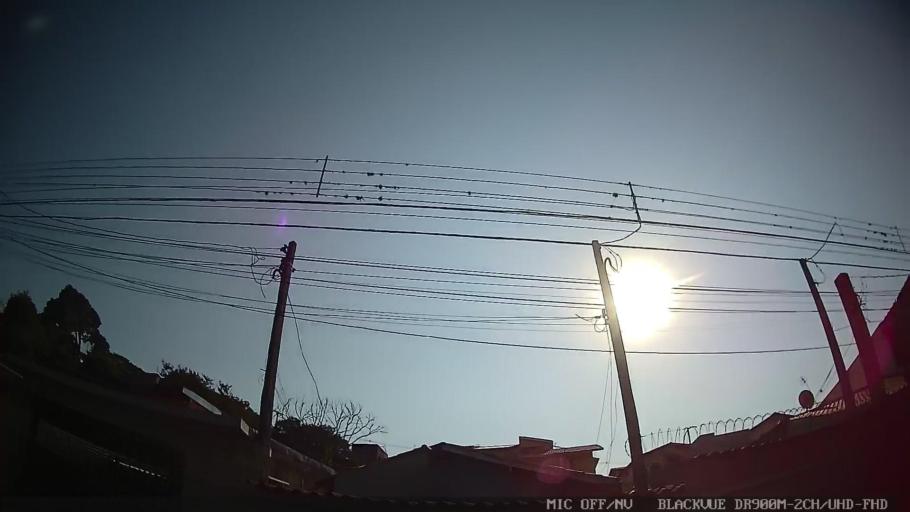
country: BR
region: Sao Paulo
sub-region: Itatiba
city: Itatiba
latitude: -22.9966
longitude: -46.8501
